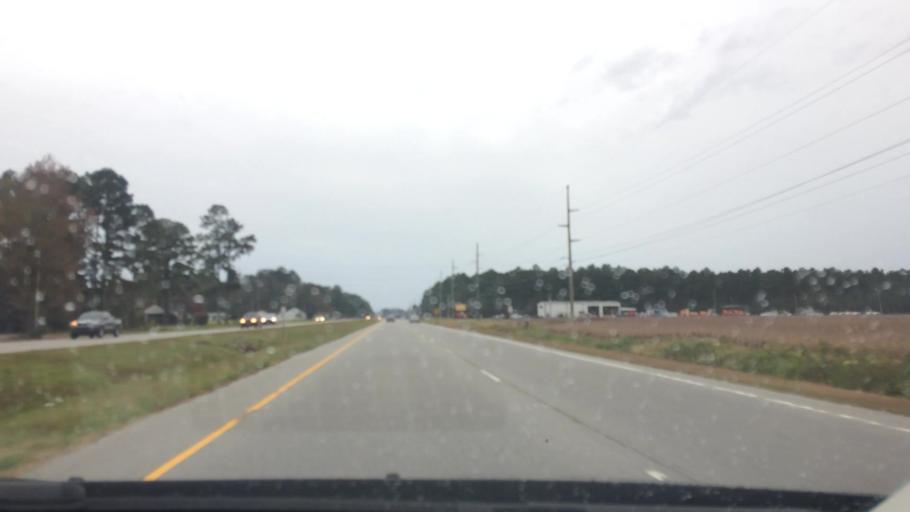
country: US
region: North Carolina
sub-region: Pitt County
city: Grifton
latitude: 35.4231
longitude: -77.4343
